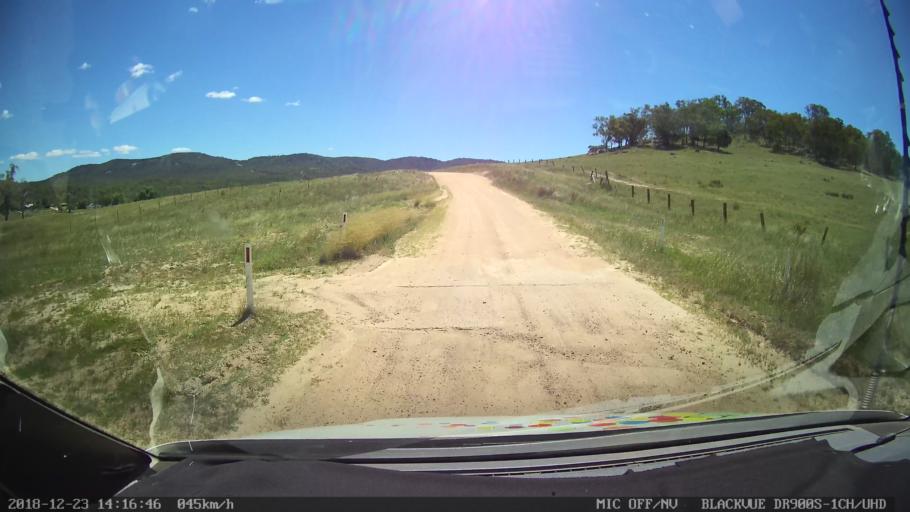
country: AU
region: New South Wales
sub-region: Tamworth Municipality
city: Manilla
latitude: -30.6602
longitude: 151.0155
